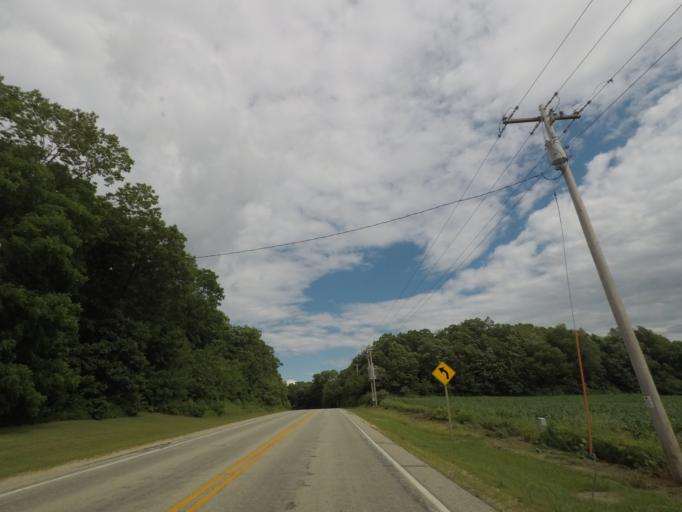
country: US
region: Wisconsin
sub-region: Dane County
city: Belleville
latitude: 42.8271
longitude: -89.4639
